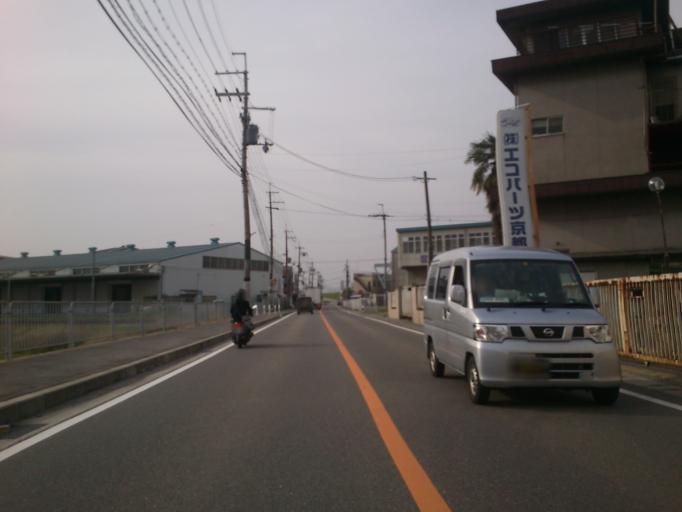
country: JP
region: Kyoto
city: Yawata
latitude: 34.8739
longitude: 135.7279
